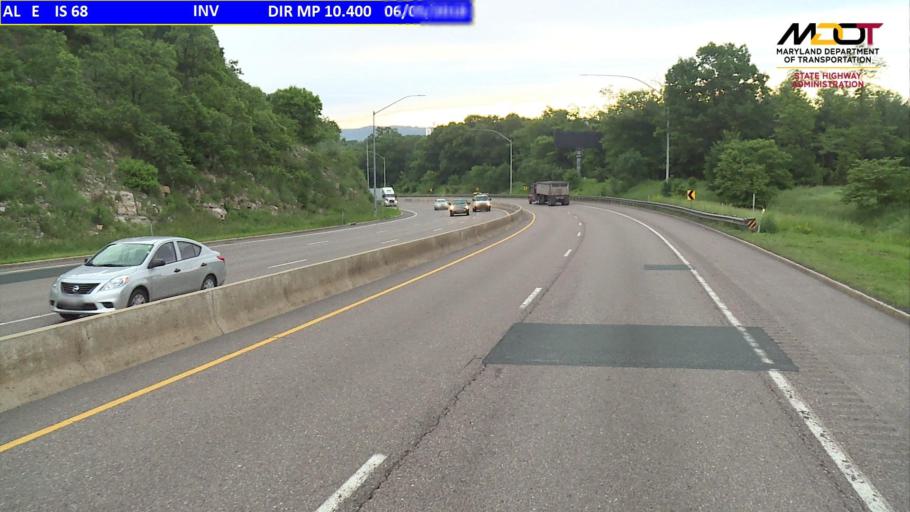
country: US
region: Maryland
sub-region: Allegany County
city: Bowling Green
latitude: 39.6405
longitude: -78.8016
